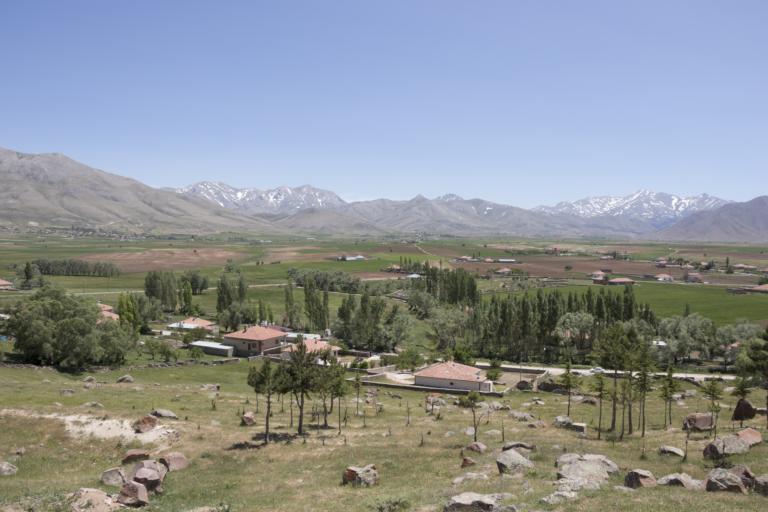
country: TR
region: Kayseri
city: Toklar
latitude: 38.4632
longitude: 36.0819
